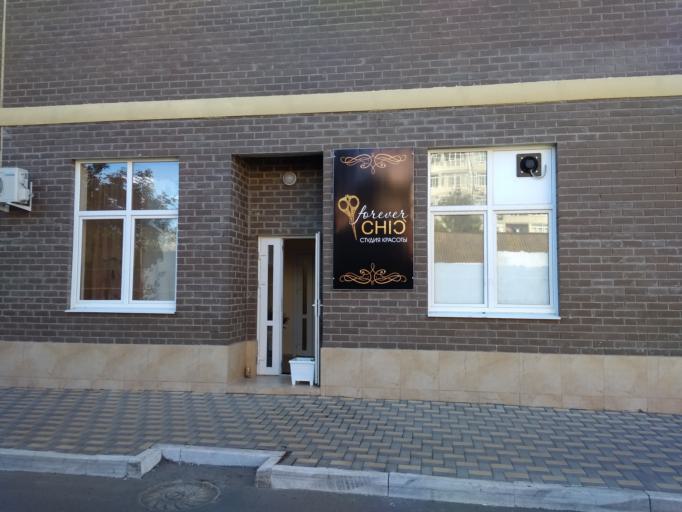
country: RU
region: Krasnodarskiy
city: Krasnodar
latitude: 45.0793
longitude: 39.0030
